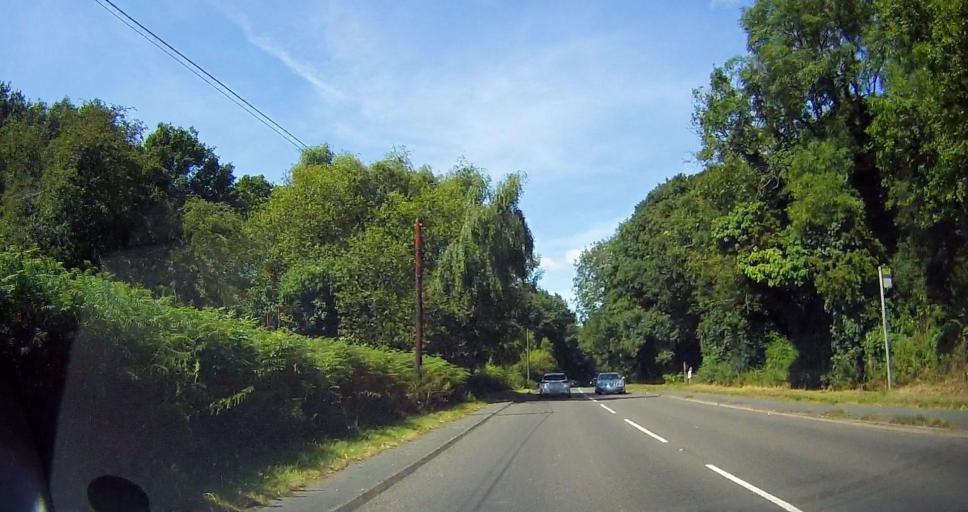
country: GB
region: England
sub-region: Shropshire
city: Albrighton
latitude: 52.6228
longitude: -2.2423
